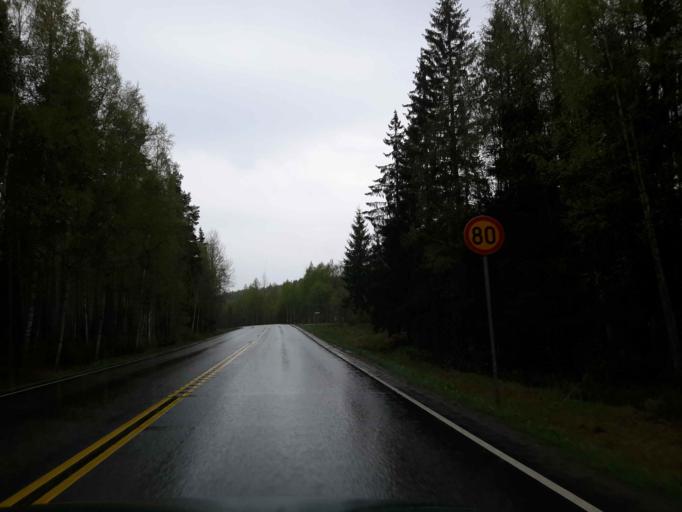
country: FI
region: Uusimaa
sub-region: Helsinki
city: Vihti
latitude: 60.3947
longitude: 24.4857
